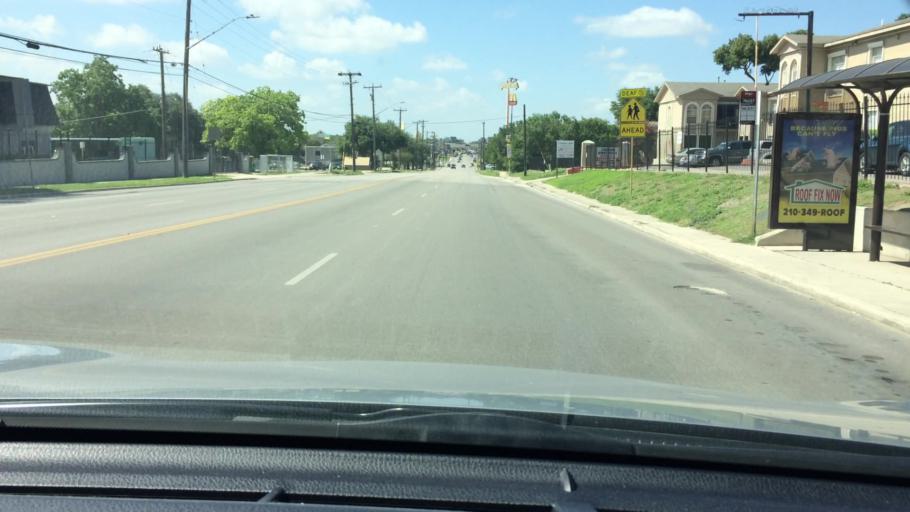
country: US
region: Texas
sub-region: Bexar County
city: Castle Hills
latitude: 29.5183
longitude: -98.5352
